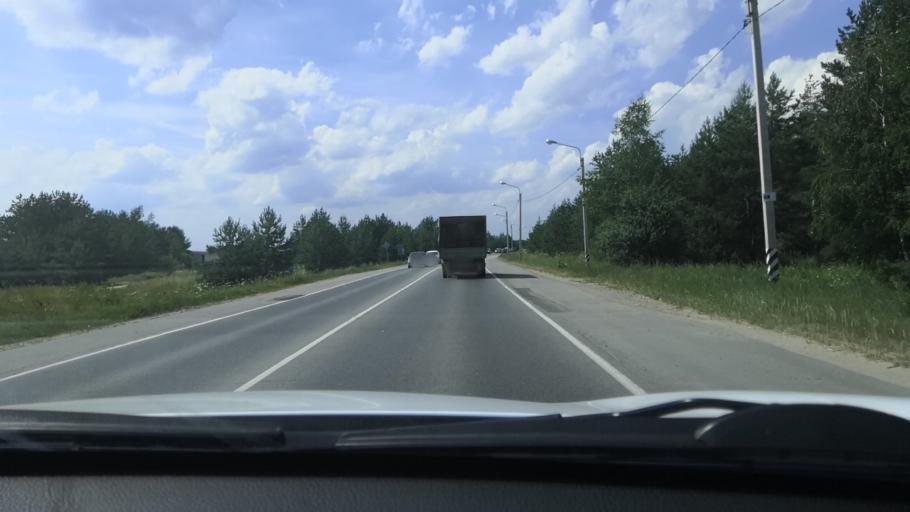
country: RU
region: Rjazan
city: Murmino
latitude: 54.6297
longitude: 39.9556
